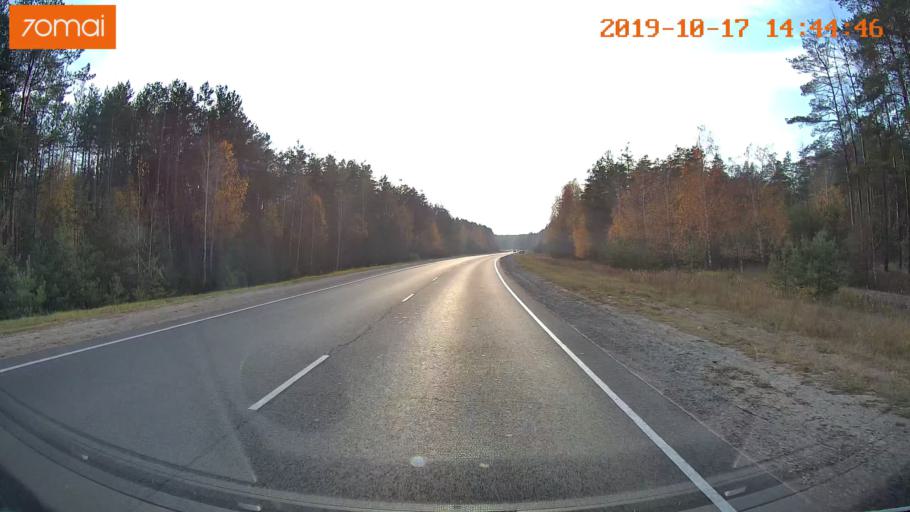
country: RU
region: Rjazan
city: Solotcha
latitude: 54.8082
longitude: 39.8873
